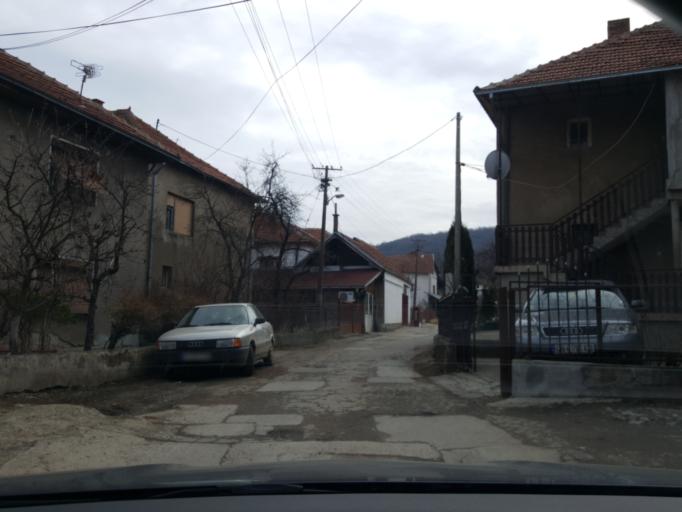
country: RS
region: Central Serbia
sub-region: Pirotski Okrug
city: Dimitrovgrad
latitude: 43.0099
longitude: 22.7526
